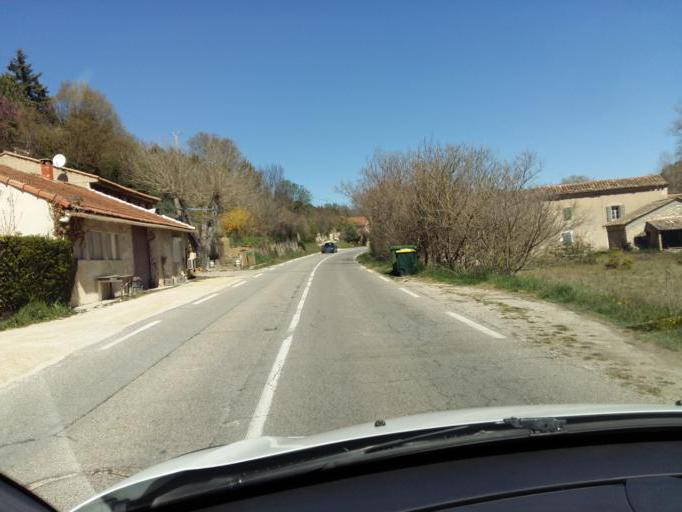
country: FR
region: Provence-Alpes-Cote d'Azur
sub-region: Departement du Vaucluse
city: Apt
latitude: 43.8823
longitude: 5.4213
